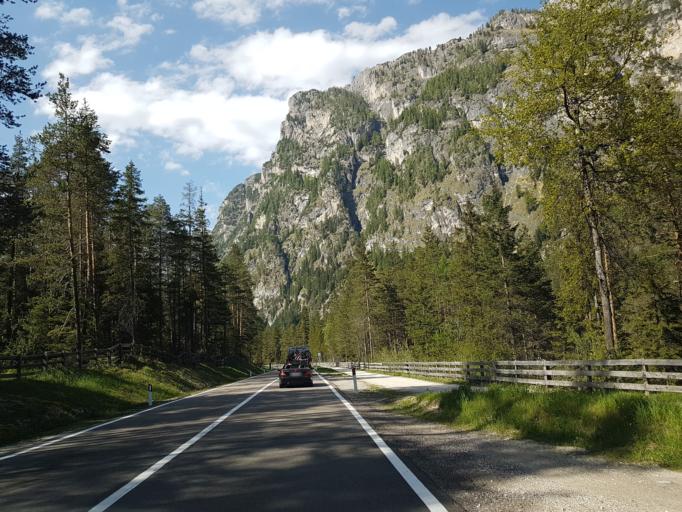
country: IT
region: Trentino-Alto Adige
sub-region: Bolzano
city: Dobbiaco
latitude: 46.6569
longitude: 12.2257
